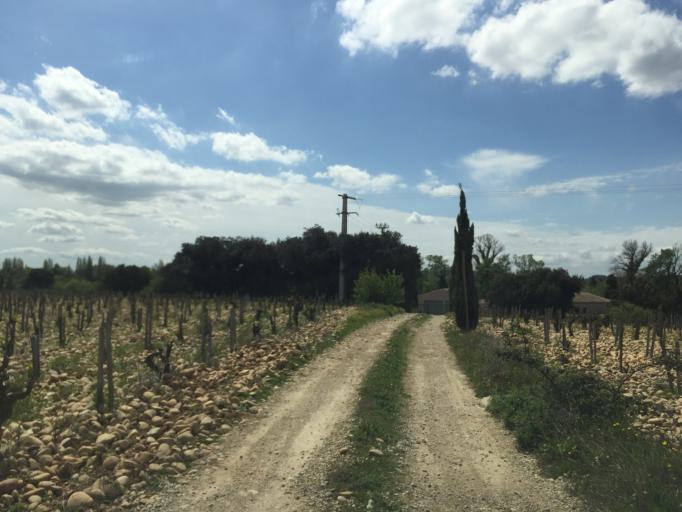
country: FR
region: Provence-Alpes-Cote d'Azur
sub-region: Departement du Vaucluse
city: Chateauneuf-du-Pape
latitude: 44.0399
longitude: 4.8314
